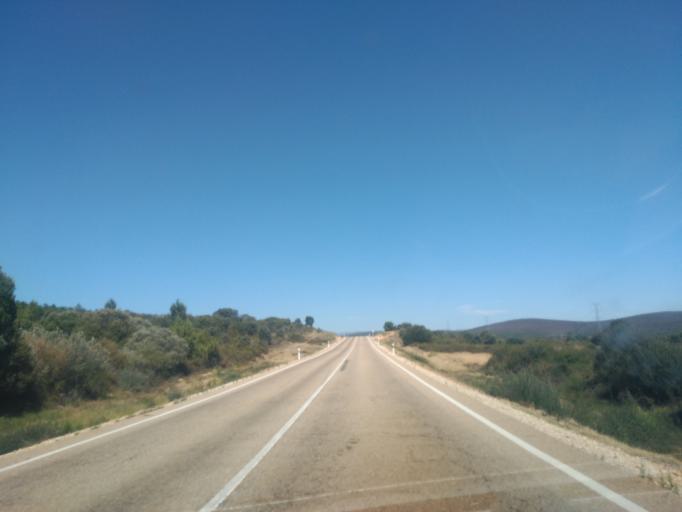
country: ES
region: Castille and Leon
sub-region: Provincia de Zamora
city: Ferreras de Abajo
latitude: 41.8830
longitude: -6.0220
